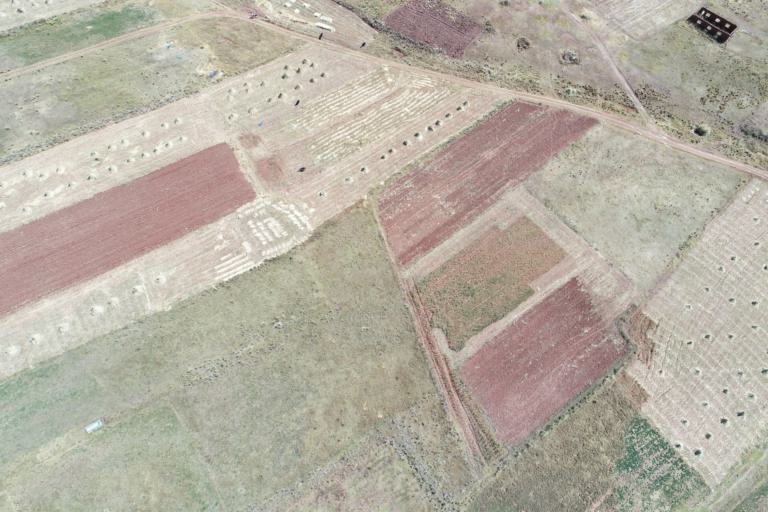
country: BO
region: La Paz
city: Tiahuanaco
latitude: -16.6021
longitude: -68.7745
